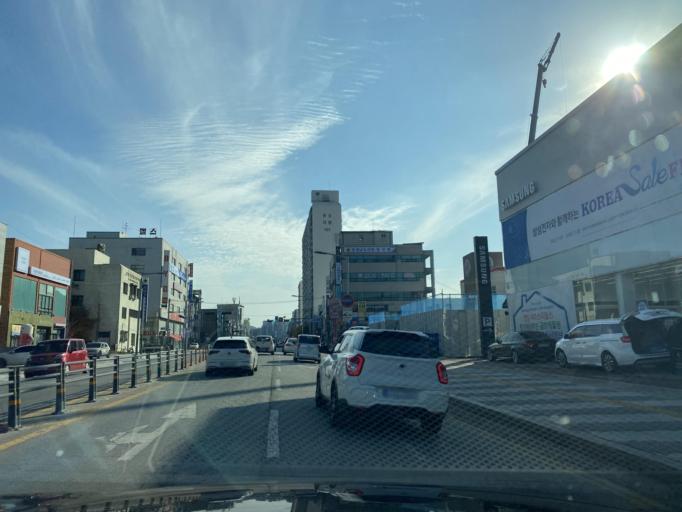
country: KR
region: Chungcheongnam-do
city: Cheonan
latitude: 36.8044
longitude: 127.1588
